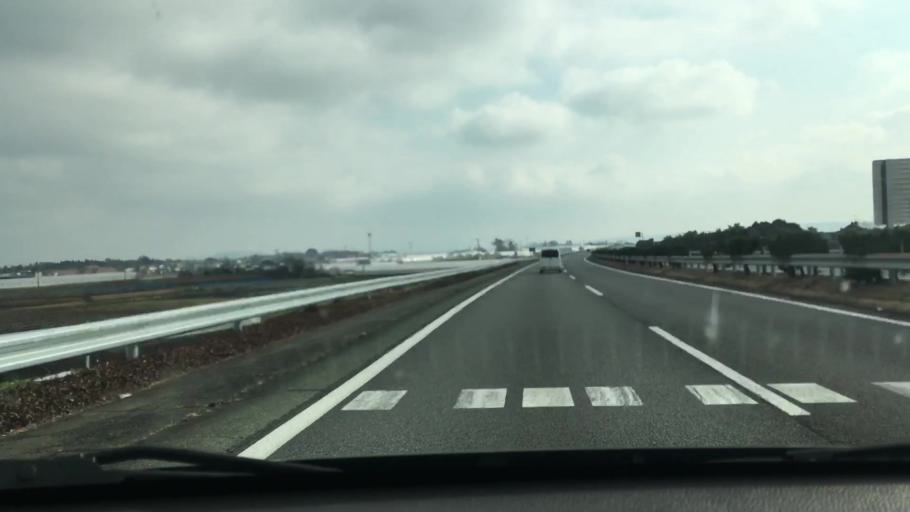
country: JP
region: Kumamoto
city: Ueki
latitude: 32.8865
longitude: 130.7246
